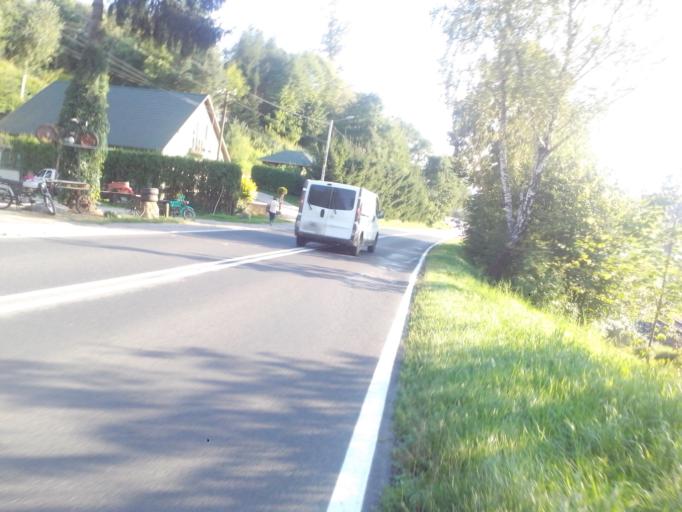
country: PL
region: Subcarpathian Voivodeship
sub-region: Powiat strzyzowski
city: Strzyzow
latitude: 49.8835
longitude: 21.8238
